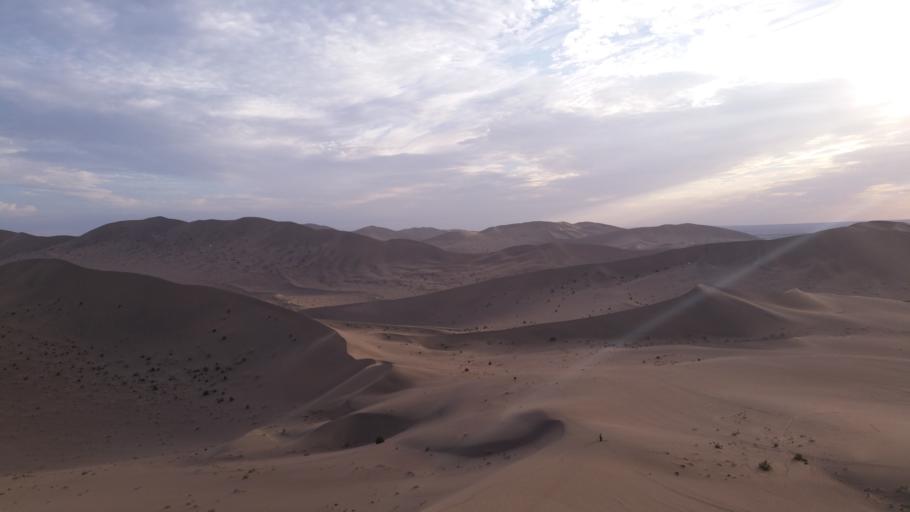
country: CN
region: Gansu Sheng
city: Yangjiaqiao
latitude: 40.0739
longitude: 94.6765
